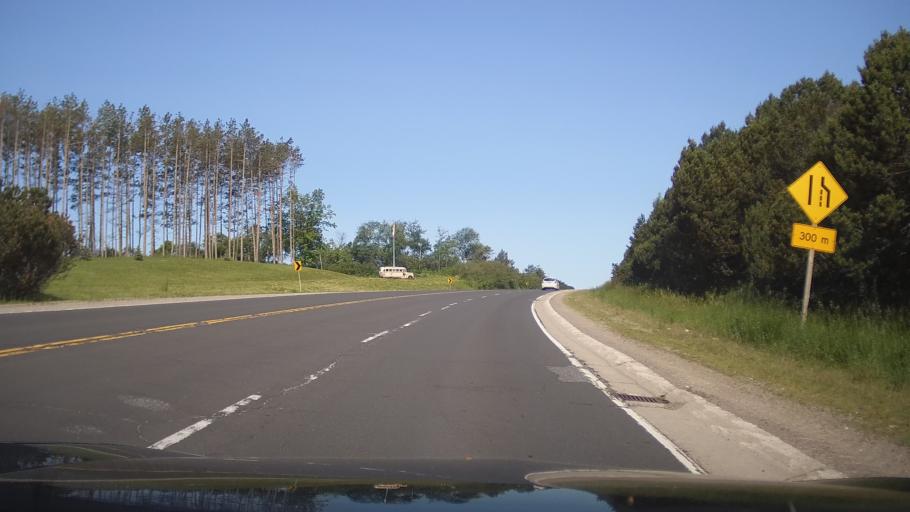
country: CA
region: Ontario
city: Omemee
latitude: 44.2926
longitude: -78.5897
